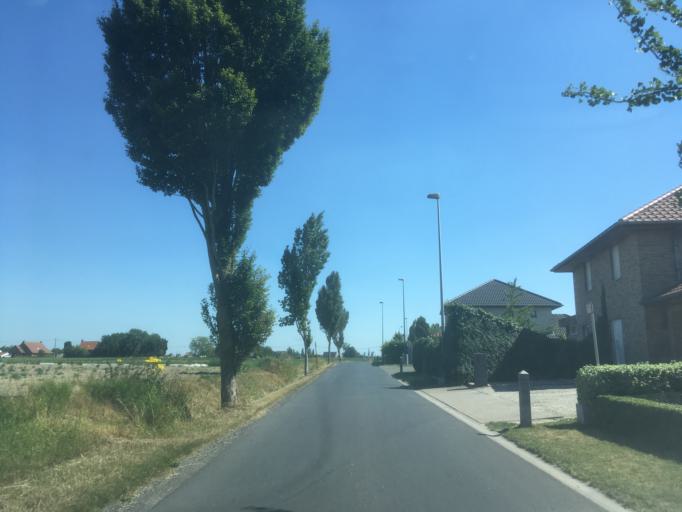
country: BE
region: Flanders
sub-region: Provincie West-Vlaanderen
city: Ardooie
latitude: 50.9441
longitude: 3.1930
